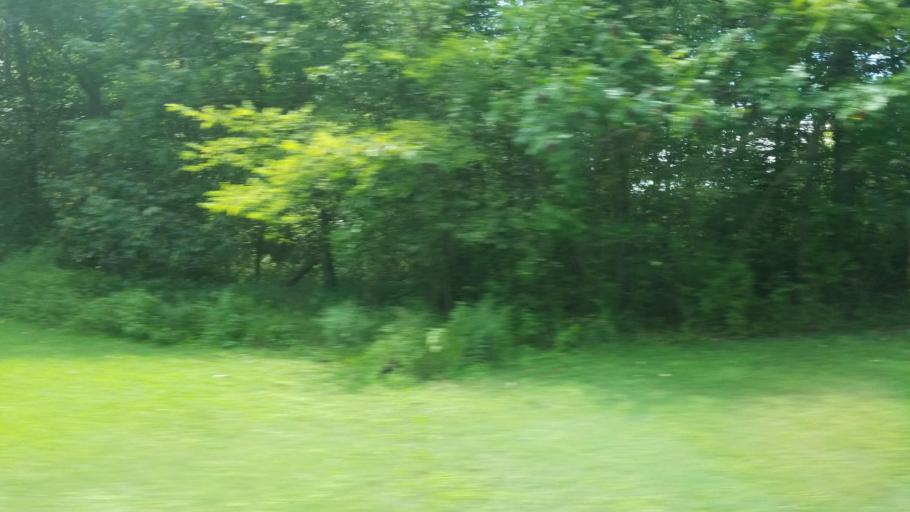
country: US
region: Illinois
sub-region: Williamson County
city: Johnston City
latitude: 37.7841
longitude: -88.8130
